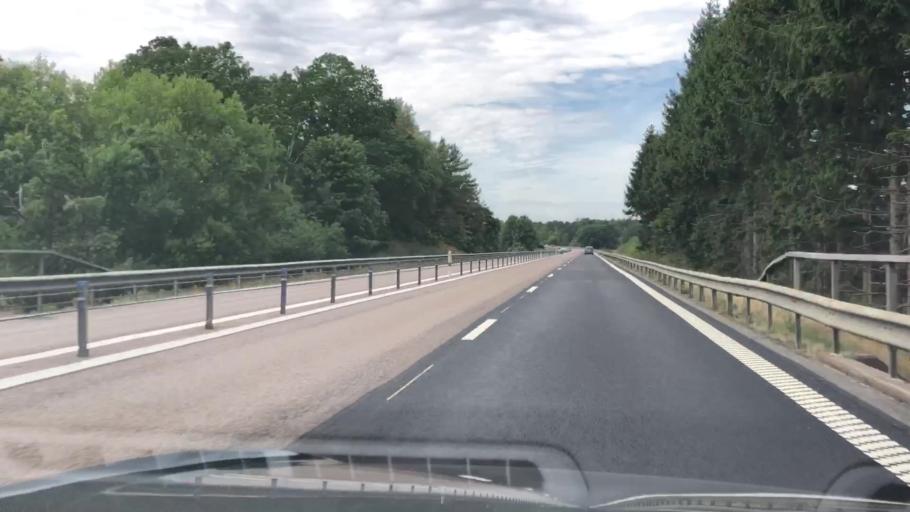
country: SE
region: Blekinge
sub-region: Ronneby Kommun
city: Brakne-Hoby
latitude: 56.2077
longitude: 15.0600
